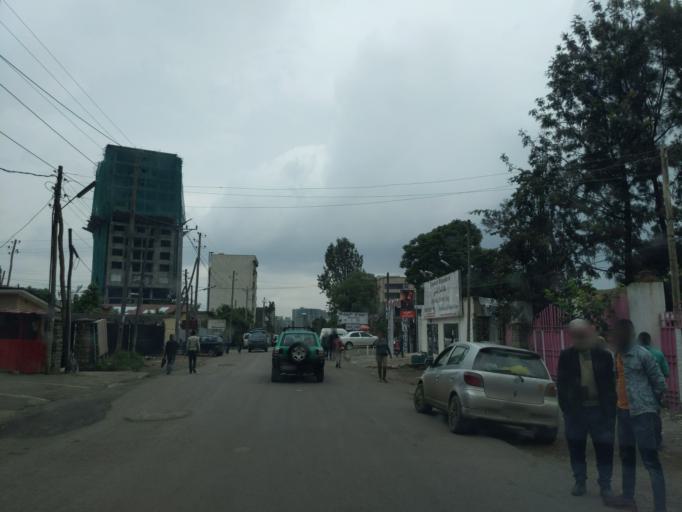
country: ET
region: Adis Abeba
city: Addis Ababa
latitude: 8.9991
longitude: 38.7681
